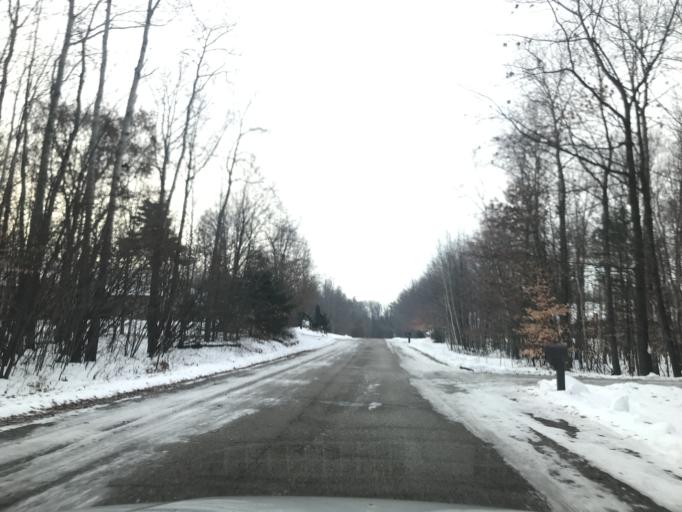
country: US
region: Wisconsin
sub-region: Brown County
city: Suamico
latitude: 44.6887
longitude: -88.0592
